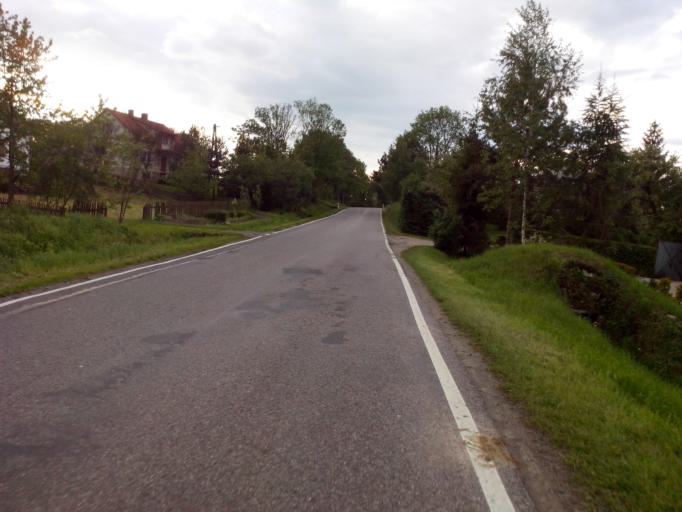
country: PL
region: Subcarpathian Voivodeship
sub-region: Powiat strzyzowski
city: Strzyzow
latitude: 49.8239
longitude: 21.8312
